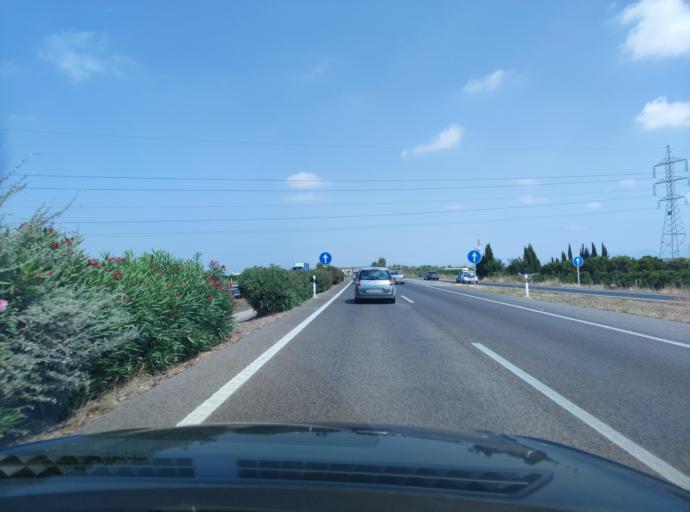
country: ES
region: Valencia
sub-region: Provincia de Castello
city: Alquerias del Nino Perdido
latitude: 39.9007
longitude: -0.1338
